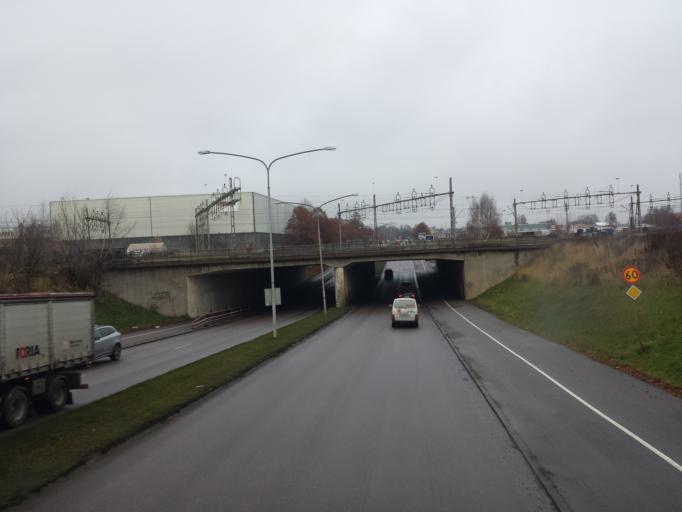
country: SE
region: OEstergoetland
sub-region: Norrkopings Kommun
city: Norrkoping
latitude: 58.5977
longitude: 16.1915
